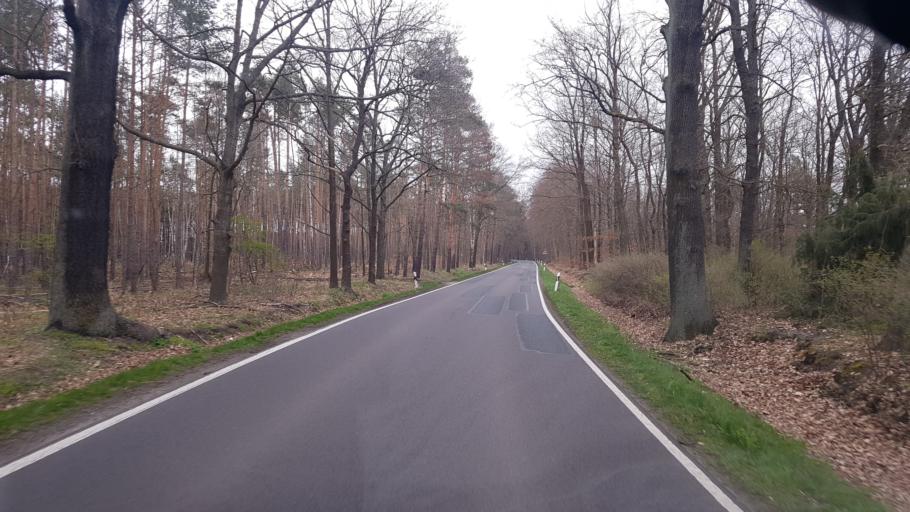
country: DE
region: Brandenburg
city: Hohenbocka
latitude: 51.4508
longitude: 13.9697
